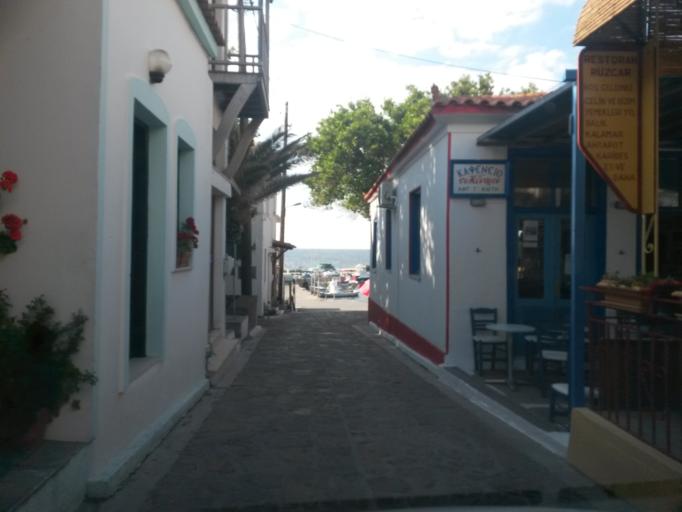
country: GR
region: North Aegean
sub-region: Nomos Lesvou
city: Eresos
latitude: 39.2114
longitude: 25.8514
